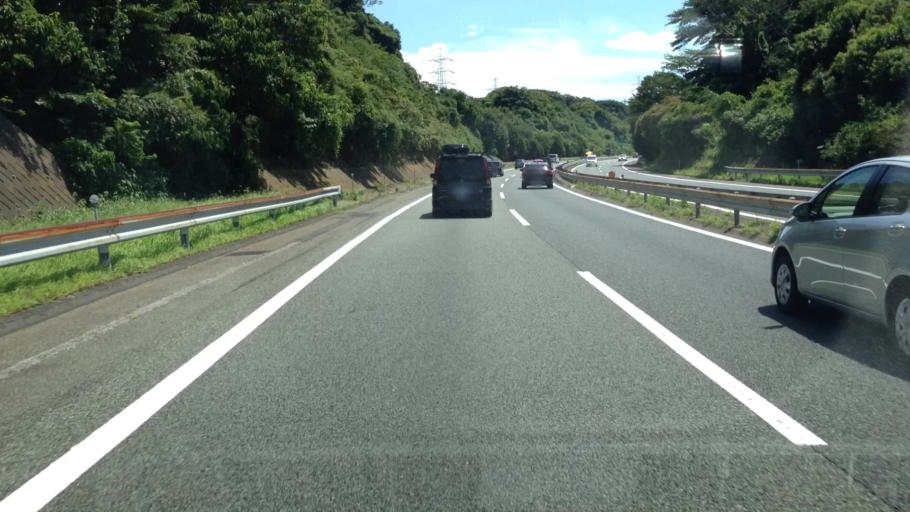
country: JP
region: Kanagawa
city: Zushi
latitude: 35.3012
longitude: 139.6150
